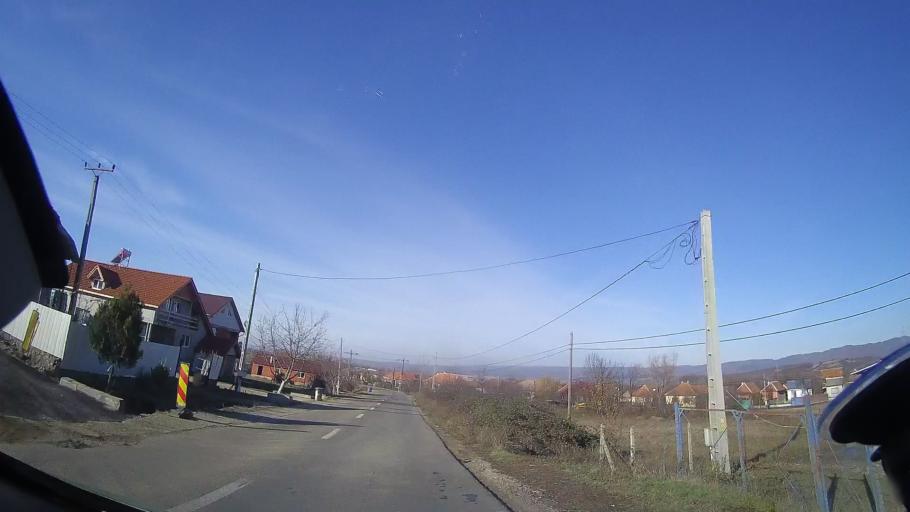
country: RO
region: Bihor
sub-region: Comuna Vadu Crisului
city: Vadu Crisului
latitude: 46.9875
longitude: 22.5290
